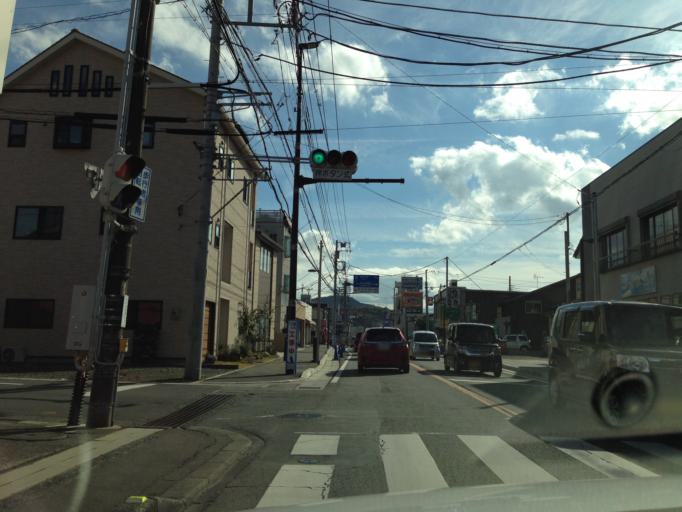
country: JP
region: Shizuoka
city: Mishima
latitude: 35.0404
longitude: 138.9457
